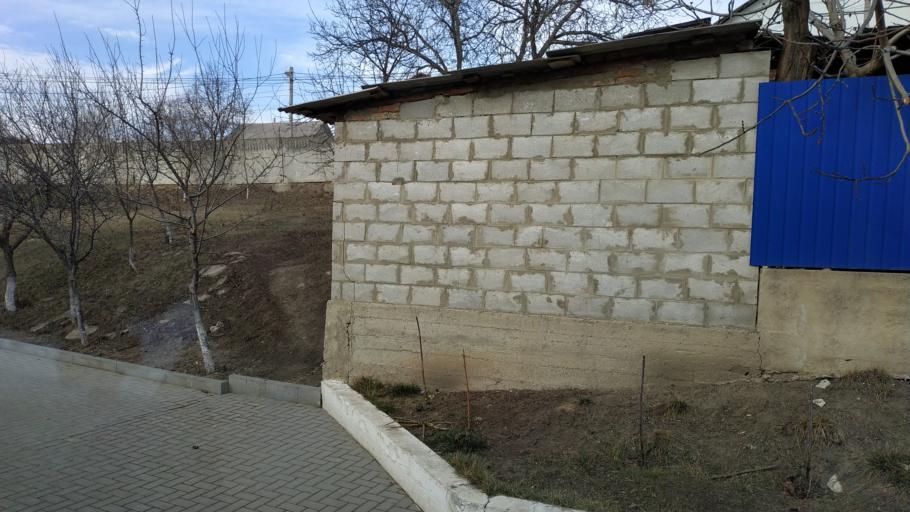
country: MD
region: Nisporeni
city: Nisporeni
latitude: 47.0834
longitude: 28.1865
